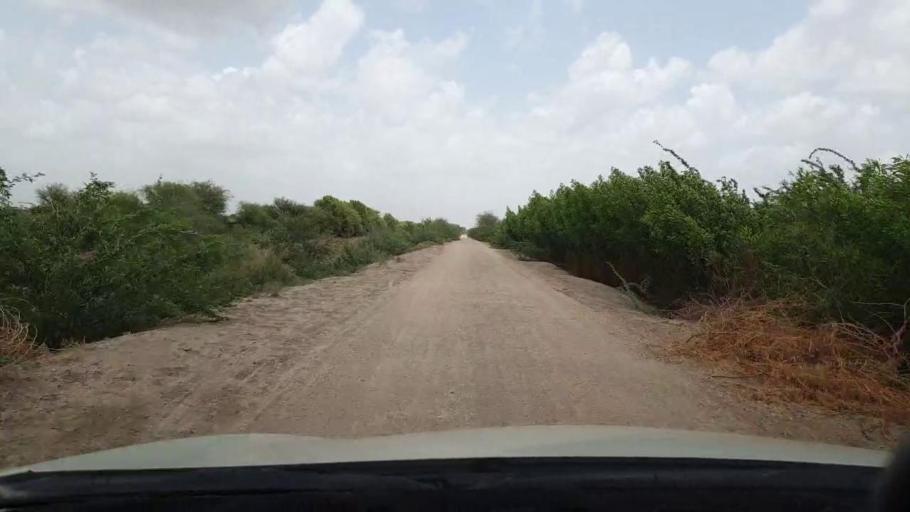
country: PK
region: Sindh
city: Kadhan
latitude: 24.3603
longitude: 68.9517
